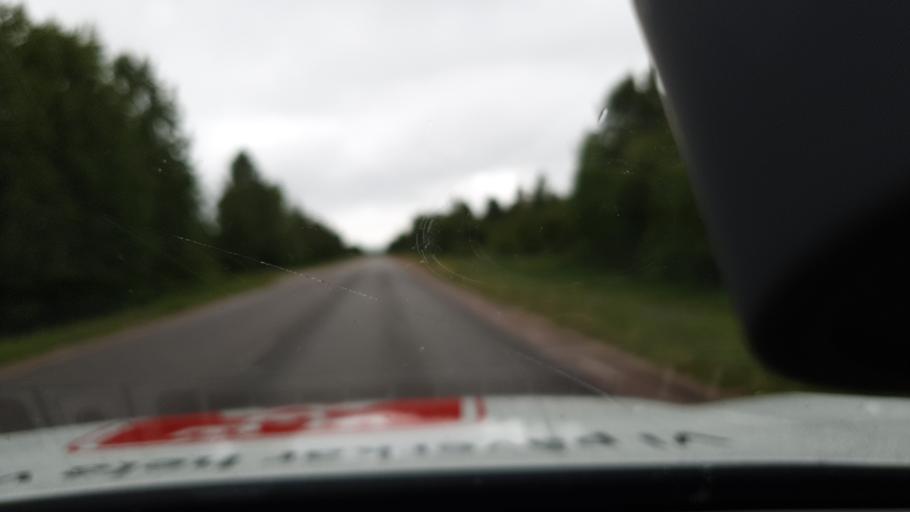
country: SE
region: Norrbotten
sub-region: Overtornea Kommun
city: OEvertornea
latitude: 66.4038
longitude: 23.6228
